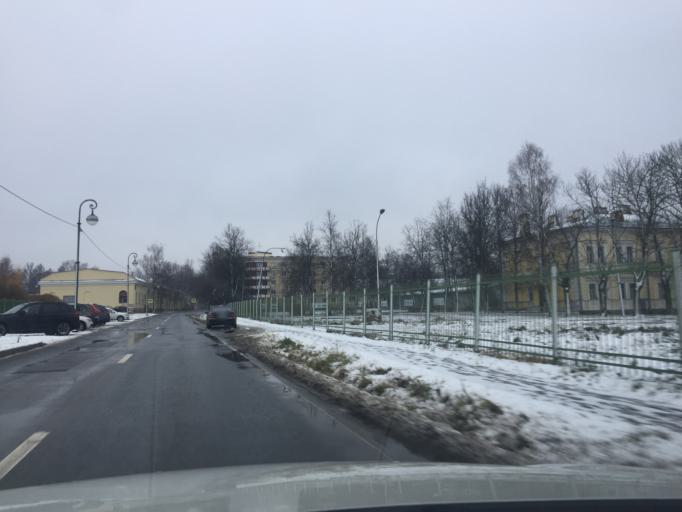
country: RU
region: St.-Petersburg
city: Pushkin
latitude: 59.7052
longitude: 30.3960
